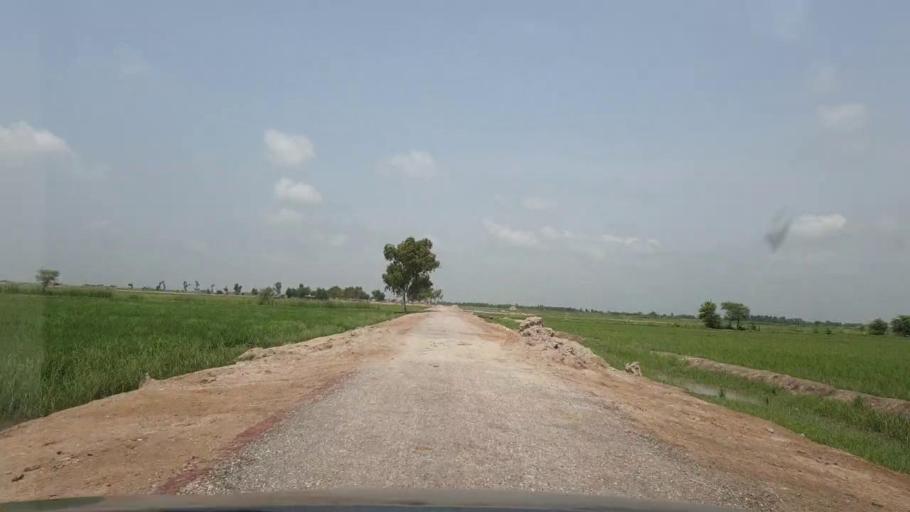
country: PK
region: Sindh
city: Ratodero
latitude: 27.9147
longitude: 68.3145
